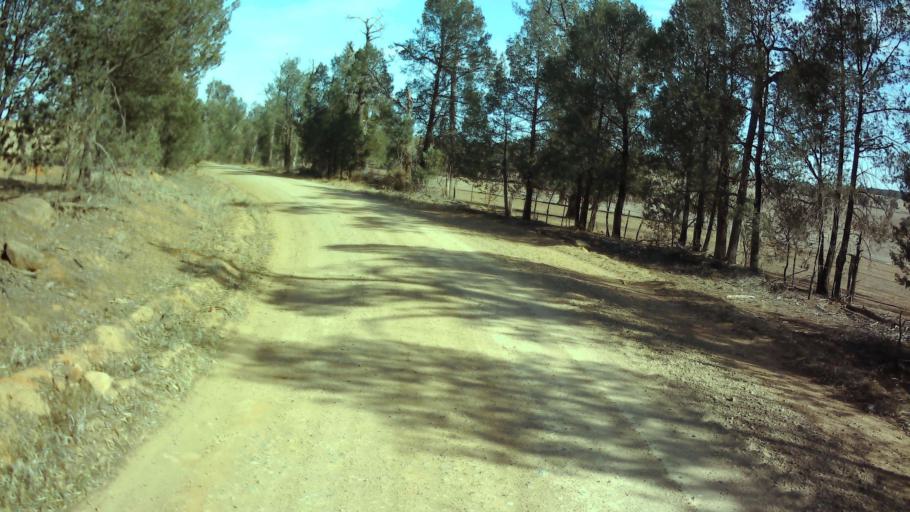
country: AU
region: New South Wales
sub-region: Weddin
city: Grenfell
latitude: -33.7668
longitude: 148.0469
